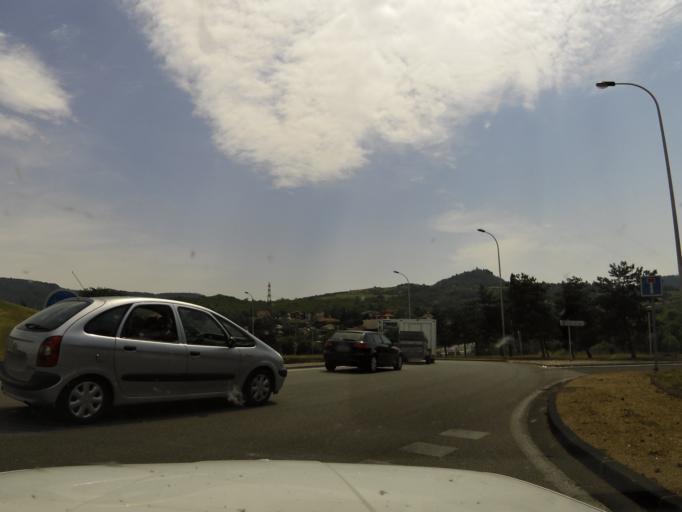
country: FR
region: Auvergne
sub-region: Departement du Puy-de-Dome
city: Beaumont
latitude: 45.7484
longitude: 3.0936
